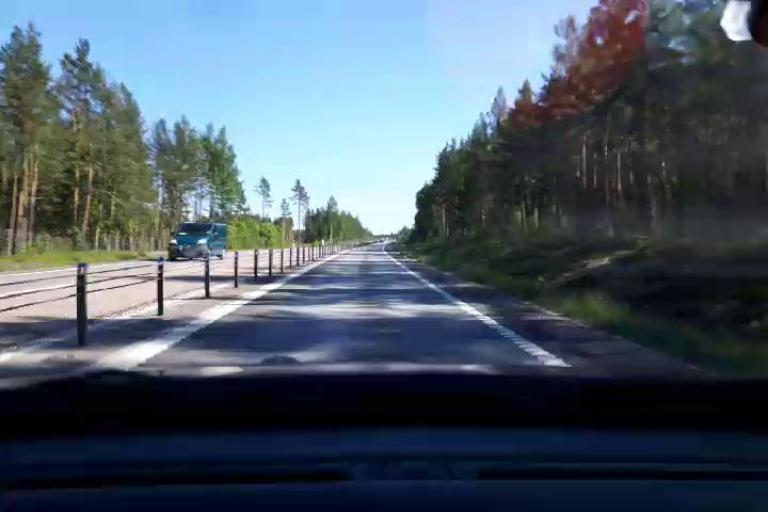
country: SE
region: Gaevleborg
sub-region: Gavle Kommun
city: Norrsundet
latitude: 60.9875
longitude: 17.0097
